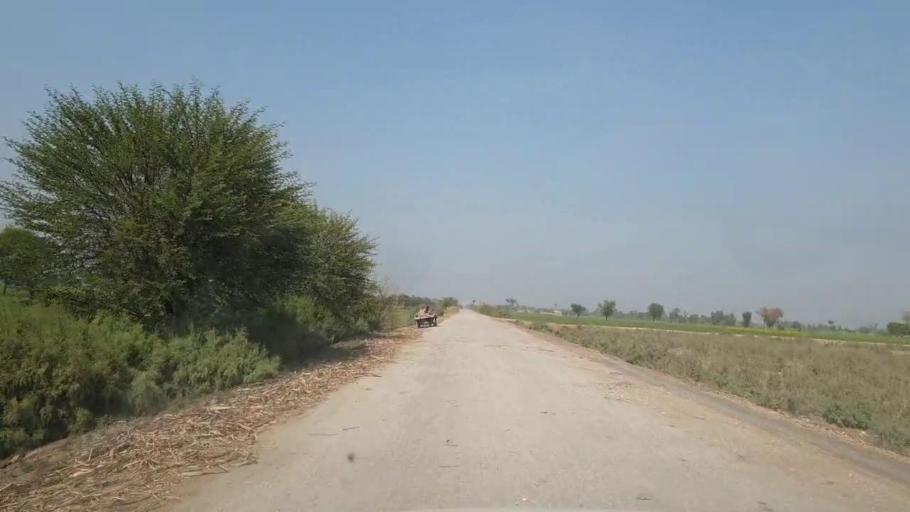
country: PK
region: Sindh
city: Mirpur Khas
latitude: 25.6738
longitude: 69.1551
